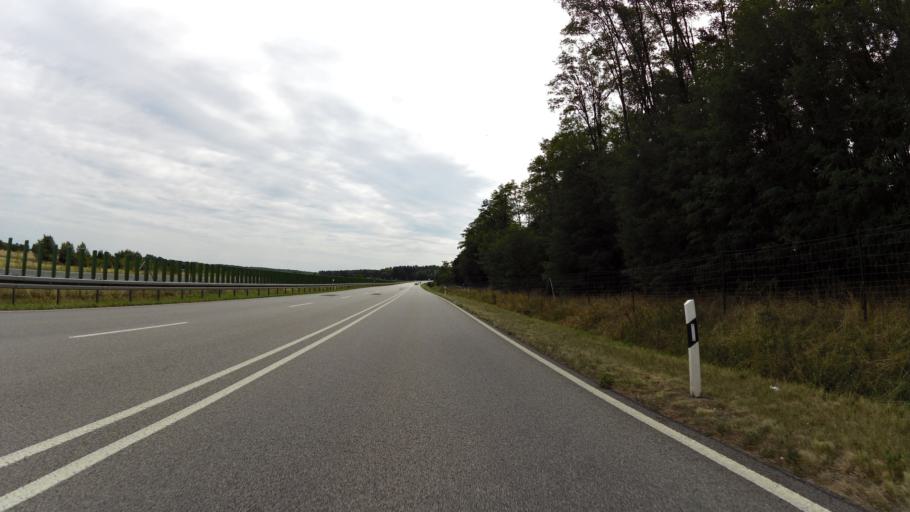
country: DE
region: Brandenburg
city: Neuzelle
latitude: 52.0469
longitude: 14.6735
